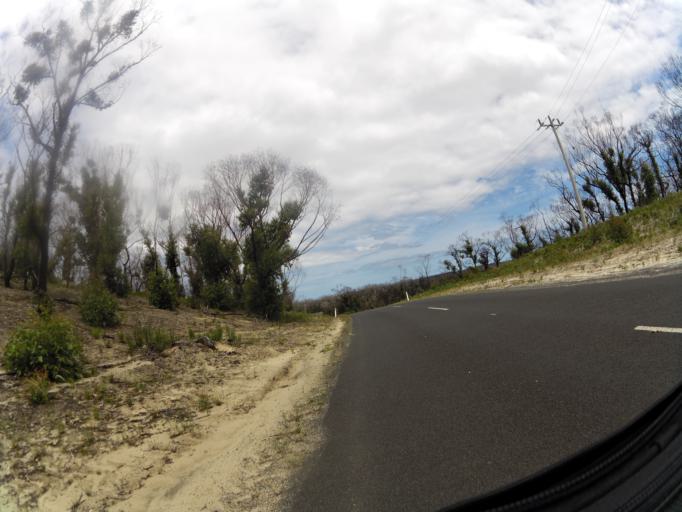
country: AU
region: Victoria
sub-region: East Gippsland
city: Lakes Entrance
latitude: -37.7943
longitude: 148.7310
